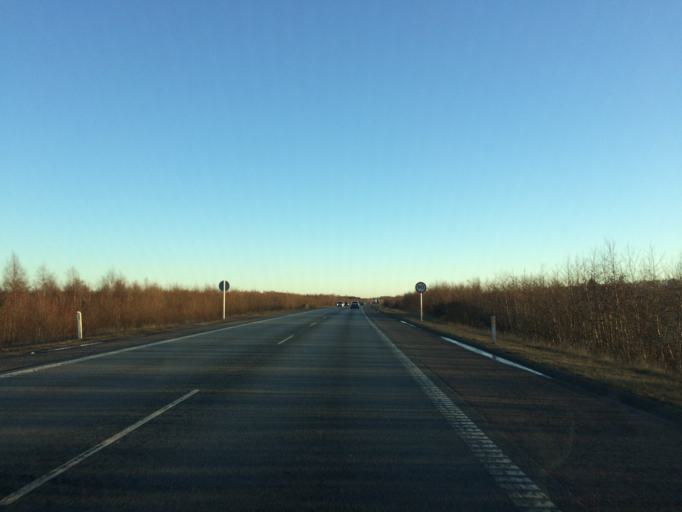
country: DK
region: Central Jutland
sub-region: Herning Kommune
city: Herning
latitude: 56.1766
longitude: 8.9843
